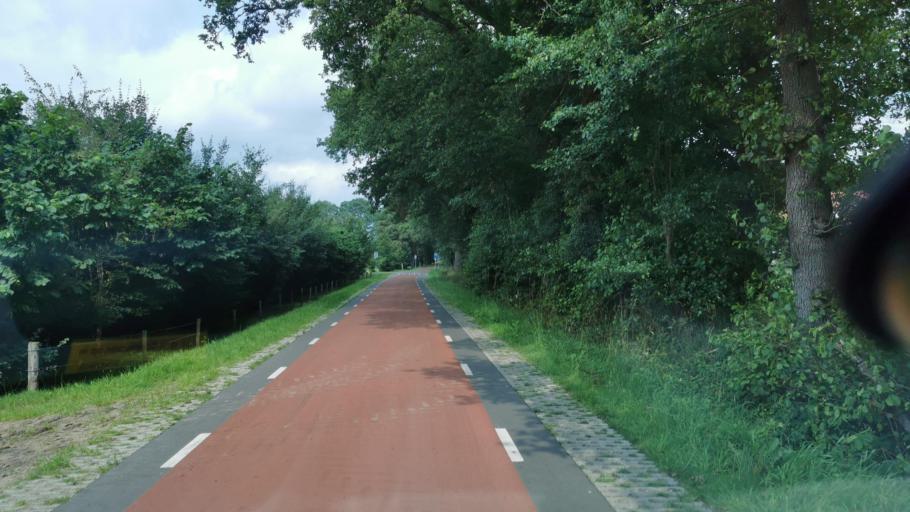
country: NL
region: Overijssel
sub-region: Gemeente Losser
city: Losser
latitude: 52.2447
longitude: 6.9755
